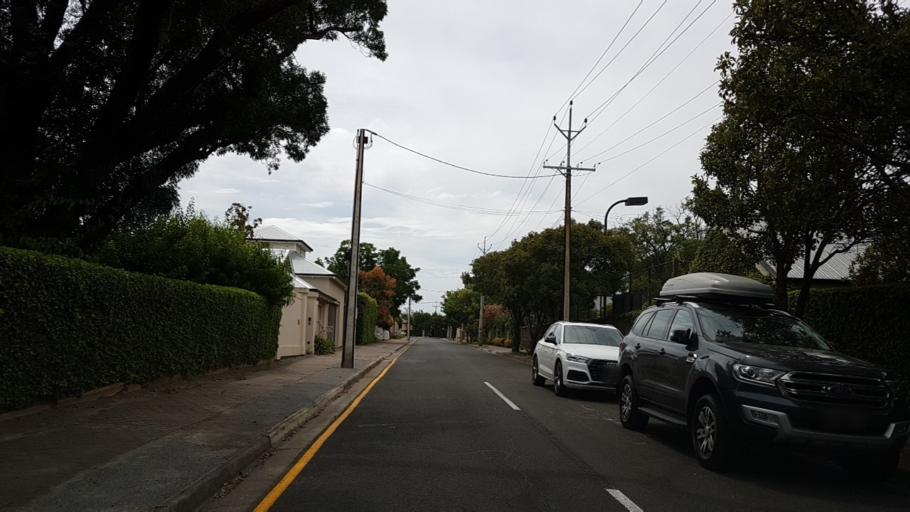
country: AU
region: South Australia
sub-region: Adelaide
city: North Adelaide
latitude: -34.8965
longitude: 138.6107
